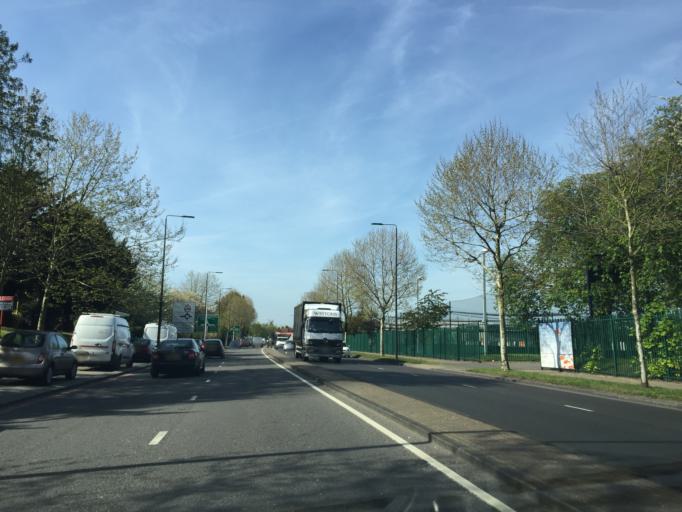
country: GB
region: England
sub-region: Greater London
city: Blackheath
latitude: 51.4477
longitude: 0.0303
